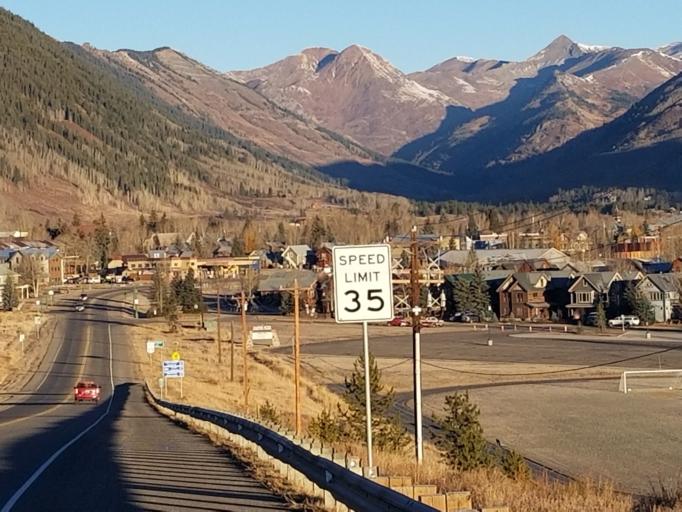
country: US
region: Colorado
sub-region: Gunnison County
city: Crested Butte
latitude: 38.8629
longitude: -106.9749
